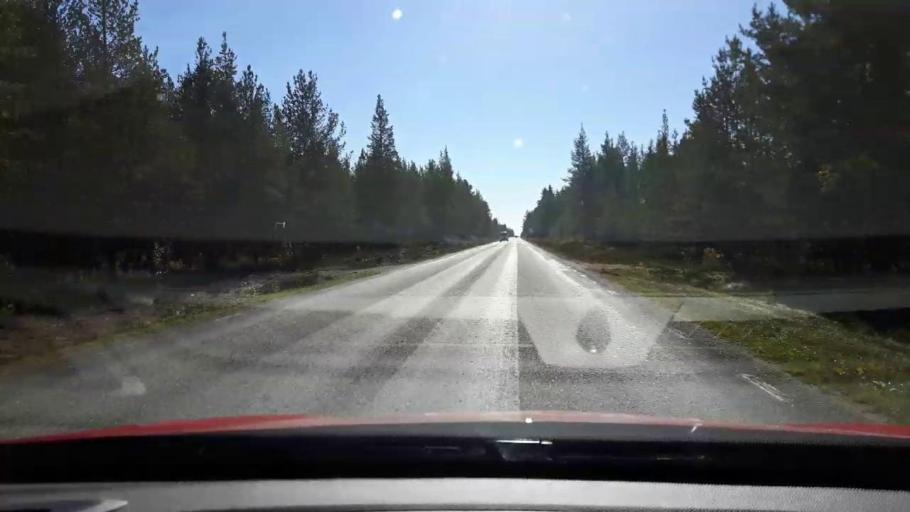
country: SE
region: Jaemtland
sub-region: Harjedalens Kommun
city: Sveg
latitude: 62.4167
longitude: 13.9128
